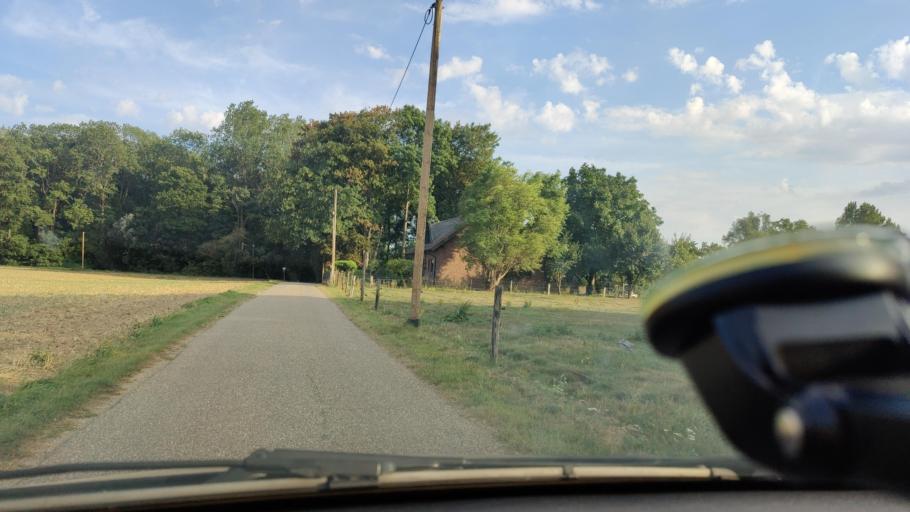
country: DE
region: North Rhine-Westphalia
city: Geldern
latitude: 51.5552
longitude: 6.3578
